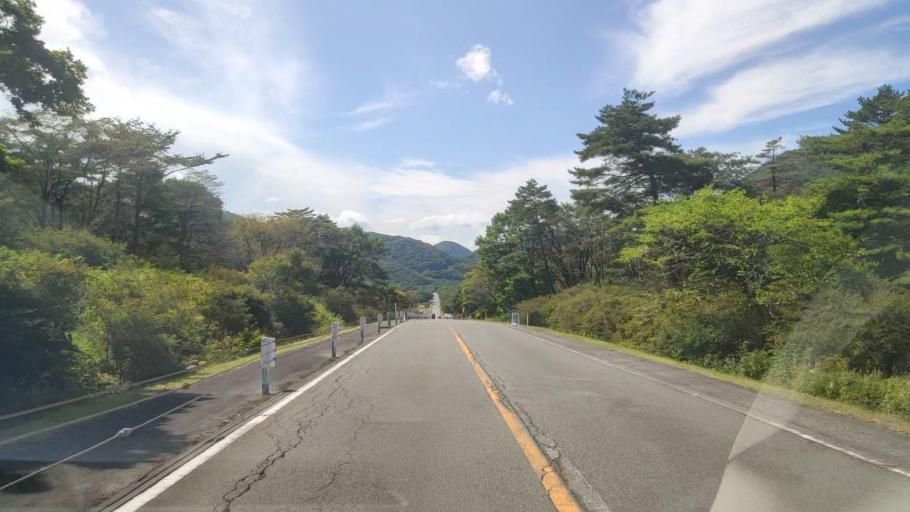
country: JP
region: Gunma
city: Shibukawa
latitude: 36.4790
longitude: 138.8929
